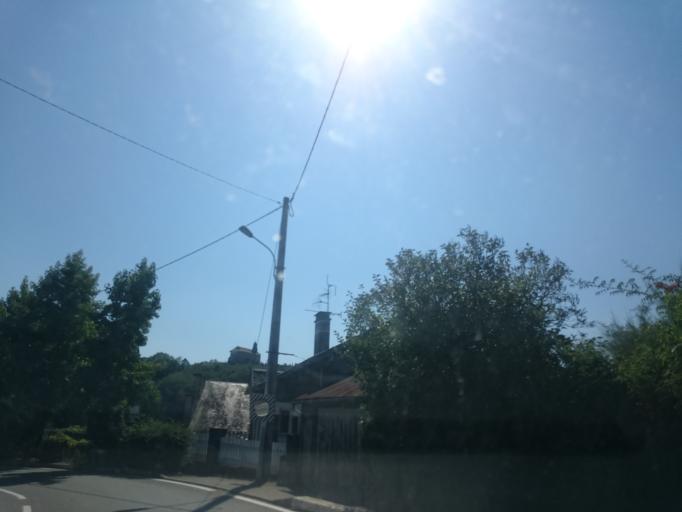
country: FR
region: Limousin
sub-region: Departement de la Correze
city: Tulle
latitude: 45.2744
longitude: 1.7768
